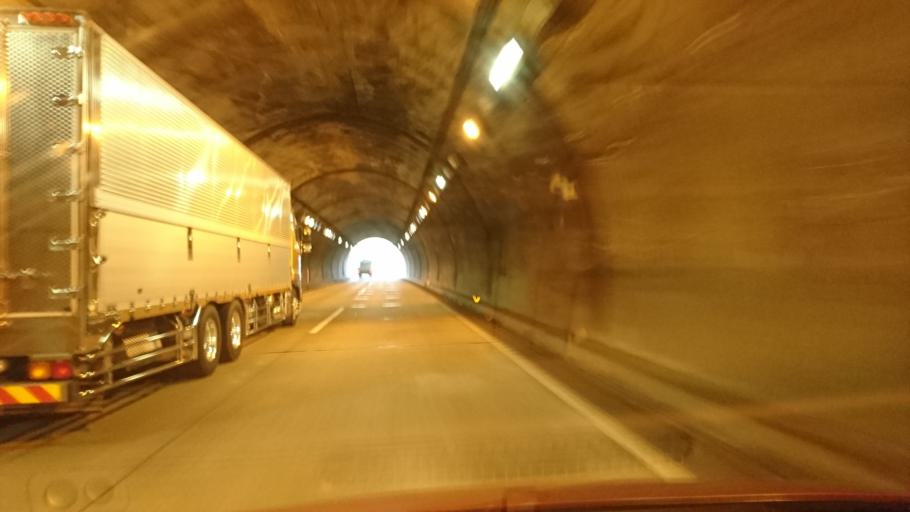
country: JP
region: Hyogo
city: Tatsunocho-tominaga
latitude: 34.8667
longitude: 134.6002
